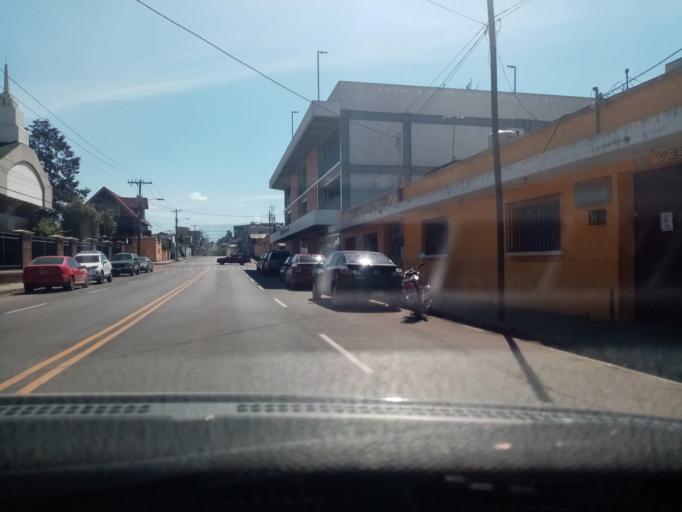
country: GT
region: Quetzaltenango
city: Quetzaltenango
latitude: 14.8464
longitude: -91.5157
